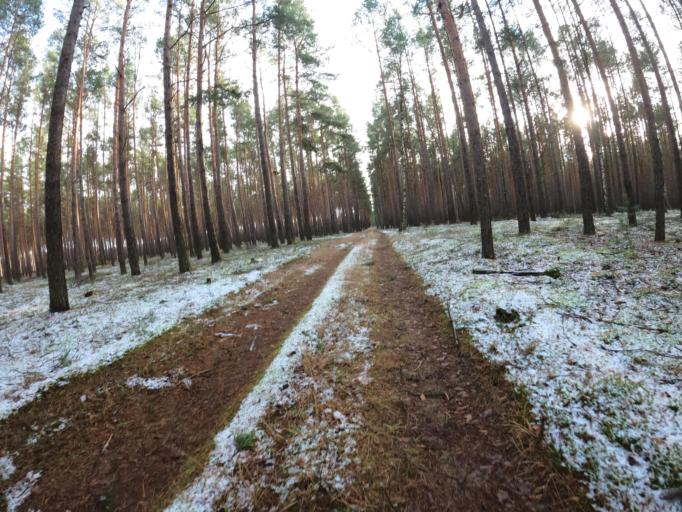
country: PL
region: Lubusz
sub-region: Powiat slubicki
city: Cybinka
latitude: 52.2408
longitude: 14.8223
